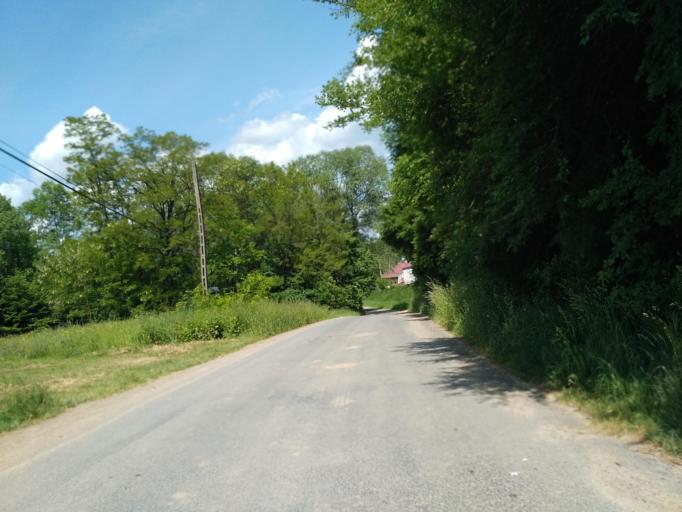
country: PL
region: Subcarpathian Voivodeship
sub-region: Powiat krosnienski
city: Dukla
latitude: 49.5960
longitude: 21.7136
